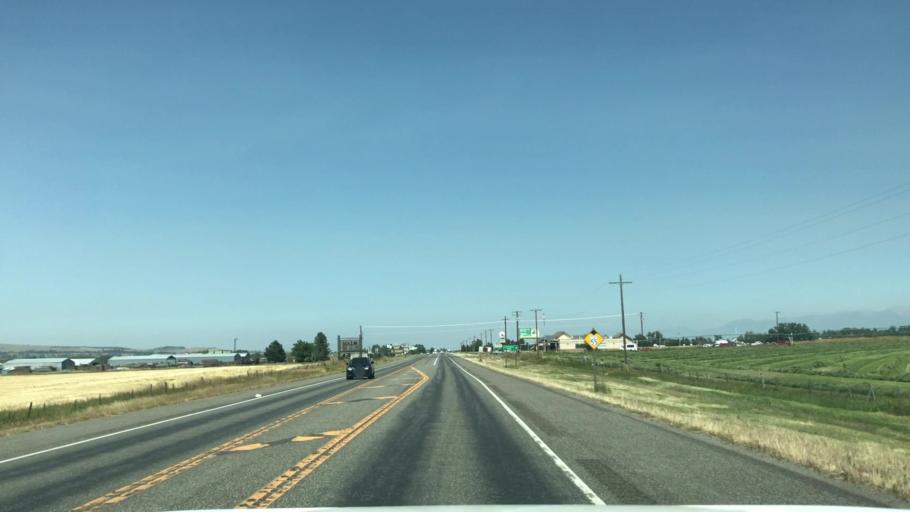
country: US
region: Montana
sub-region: Gallatin County
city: Four Corners
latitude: 45.5810
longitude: -111.1970
